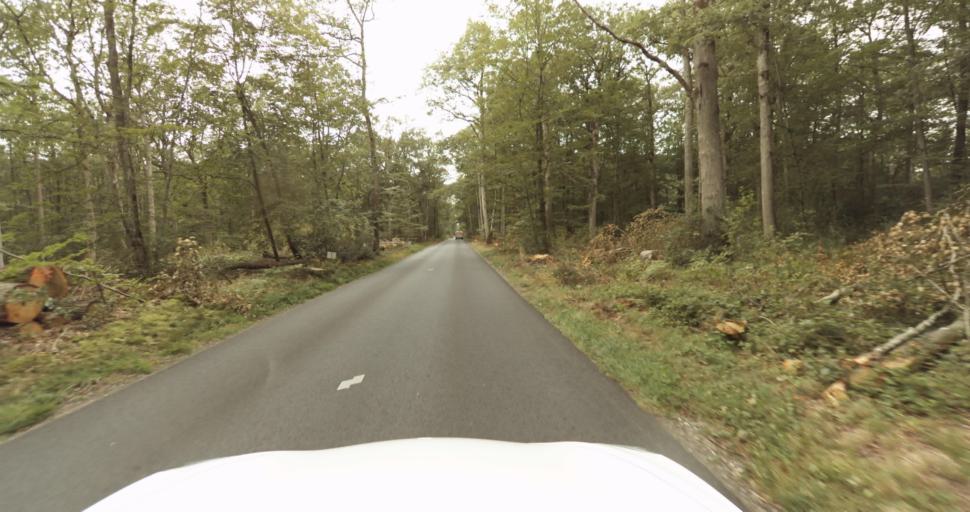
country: FR
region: Haute-Normandie
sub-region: Departement de l'Eure
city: Arnieres-sur-Iton
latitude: 48.9789
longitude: 1.0775
